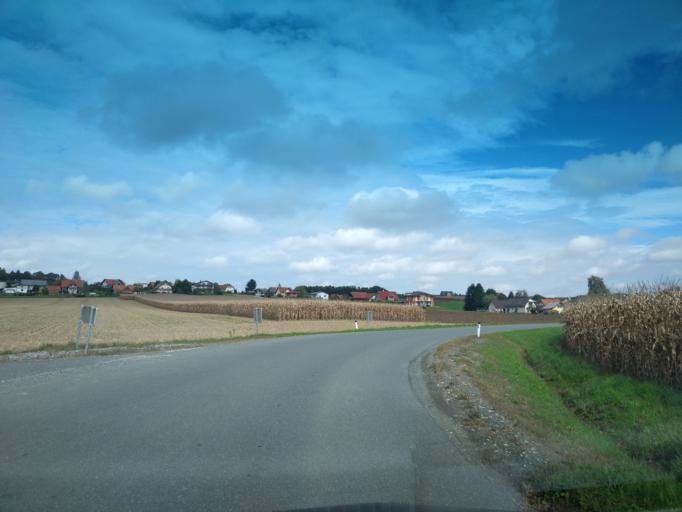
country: AT
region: Styria
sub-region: Politischer Bezirk Deutschlandsberg
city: Wettmannstatten
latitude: 46.8366
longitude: 15.3617
